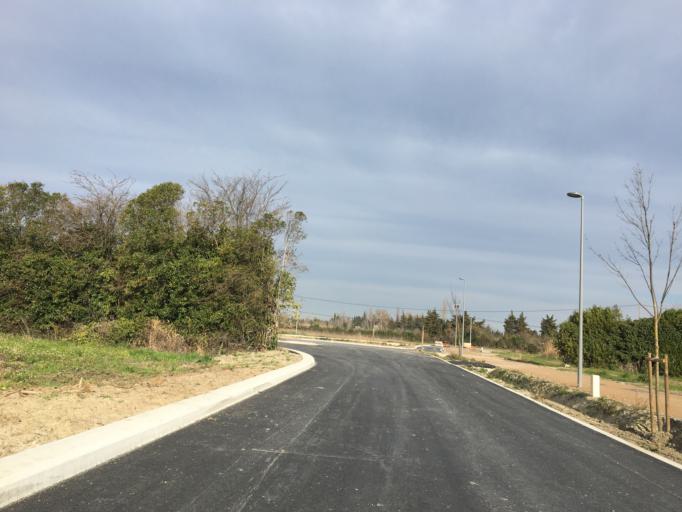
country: FR
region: Provence-Alpes-Cote d'Azur
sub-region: Departement du Vaucluse
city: Le Thor
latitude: 43.9279
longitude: 5.0165
